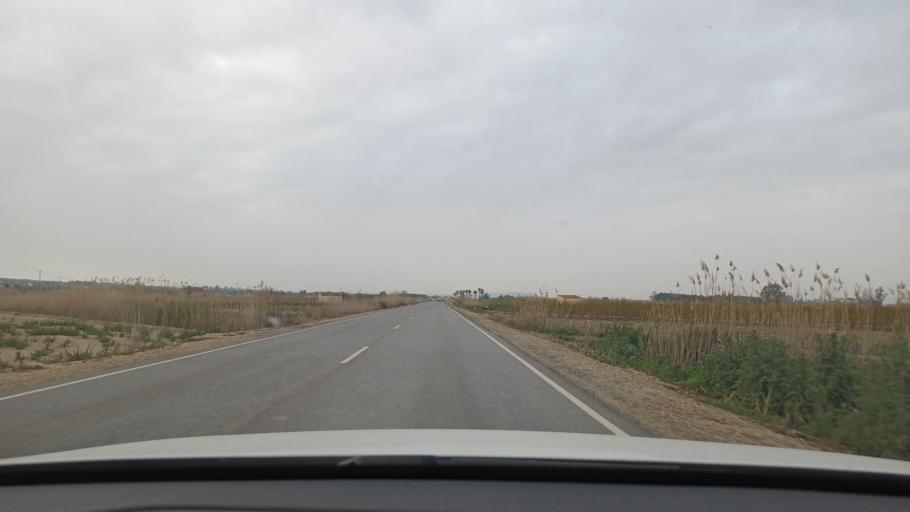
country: ES
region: Valencia
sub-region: Provincia de Alicante
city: Daya Vieja
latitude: 38.1643
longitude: -0.7028
